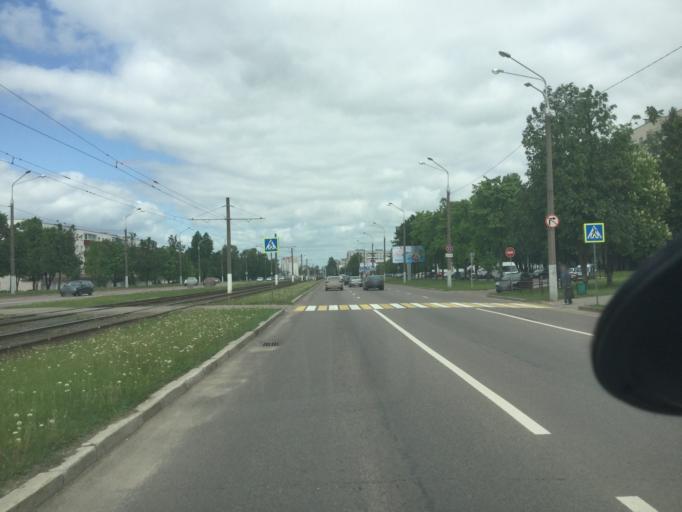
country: BY
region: Vitebsk
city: Vitebsk
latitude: 55.1804
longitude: 30.2295
